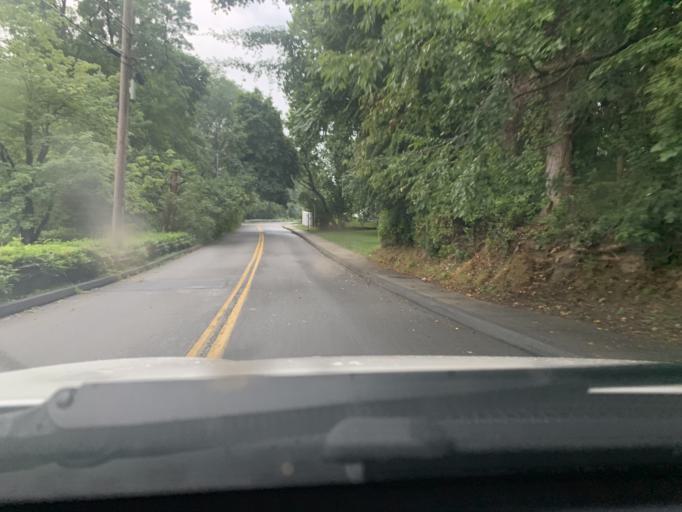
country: US
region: New York
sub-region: Westchester County
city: Ossining
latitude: 41.1699
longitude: -73.8586
